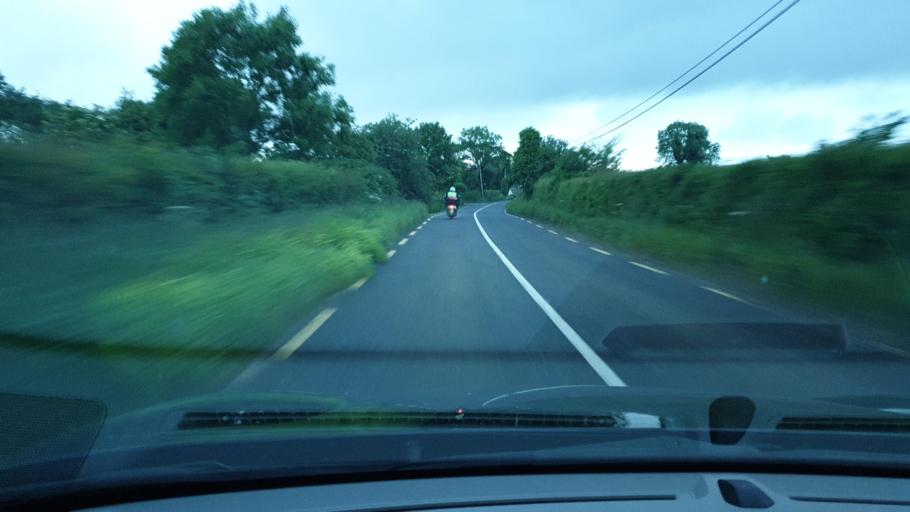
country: IE
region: Leinster
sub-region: An Mhi
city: Ashbourne
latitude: 53.5086
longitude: -6.3192
